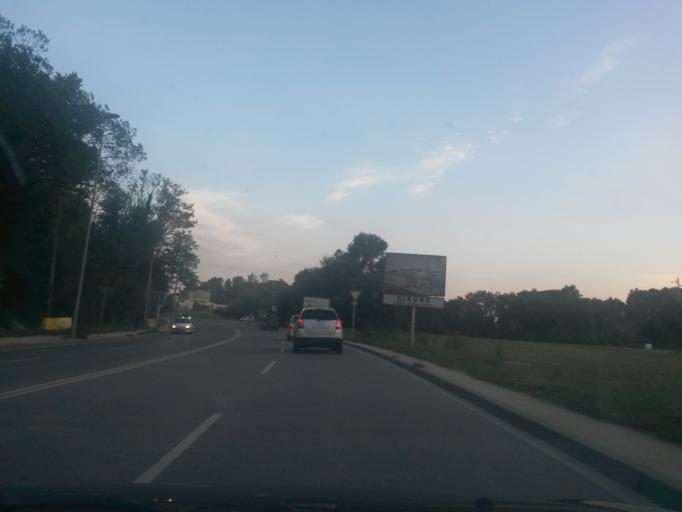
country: ES
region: Catalonia
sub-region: Provincia de Girona
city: Girona
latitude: 42.0012
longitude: 2.8163
